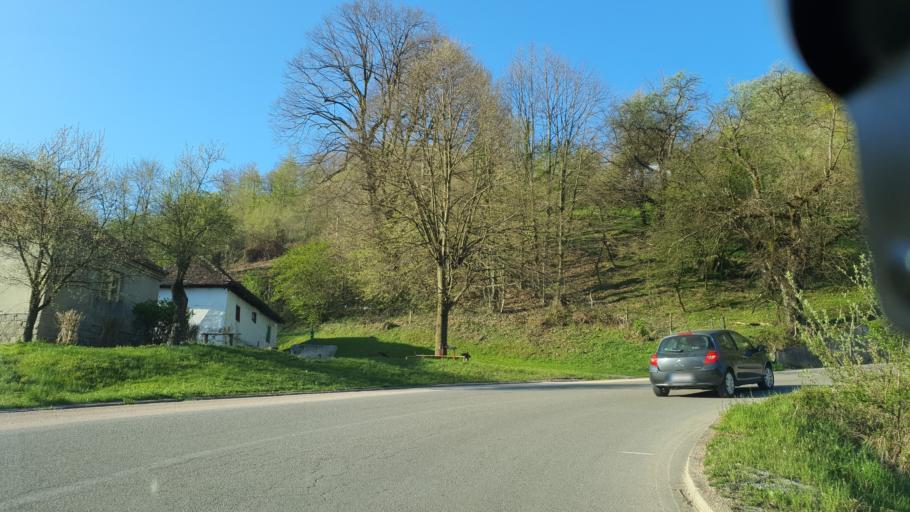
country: RS
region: Central Serbia
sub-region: Kolubarski Okrug
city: Osecina
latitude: 44.2763
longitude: 19.5256
